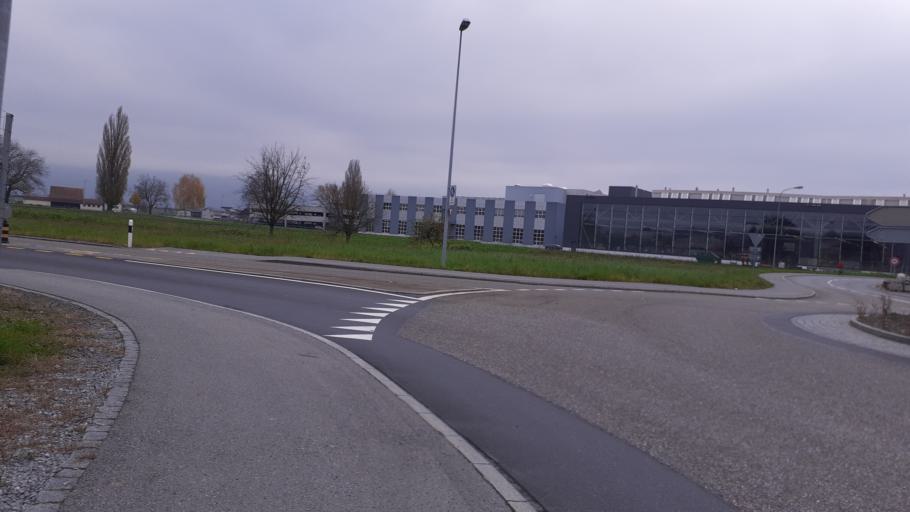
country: CH
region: Saint Gallen
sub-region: Wahlkreis Rheintal
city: Au
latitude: 47.4211
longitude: 9.6371
